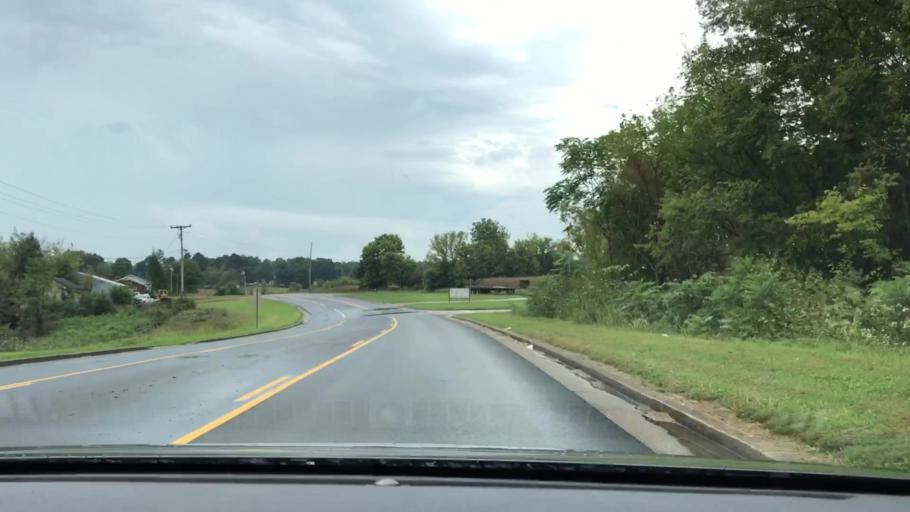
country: US
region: Tennessee
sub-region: Macon County
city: Red Boiling Springs
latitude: 36.5177
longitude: -85.8600
